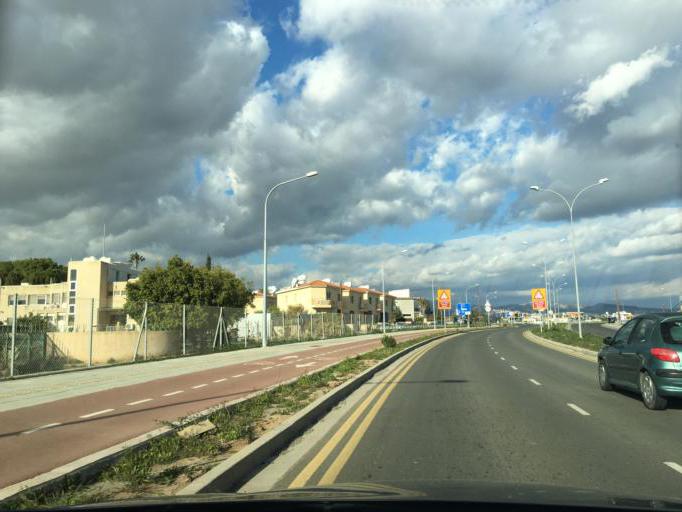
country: CY
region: Limassol
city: Pano Polemidia
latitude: 34.6787
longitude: 32.9898
